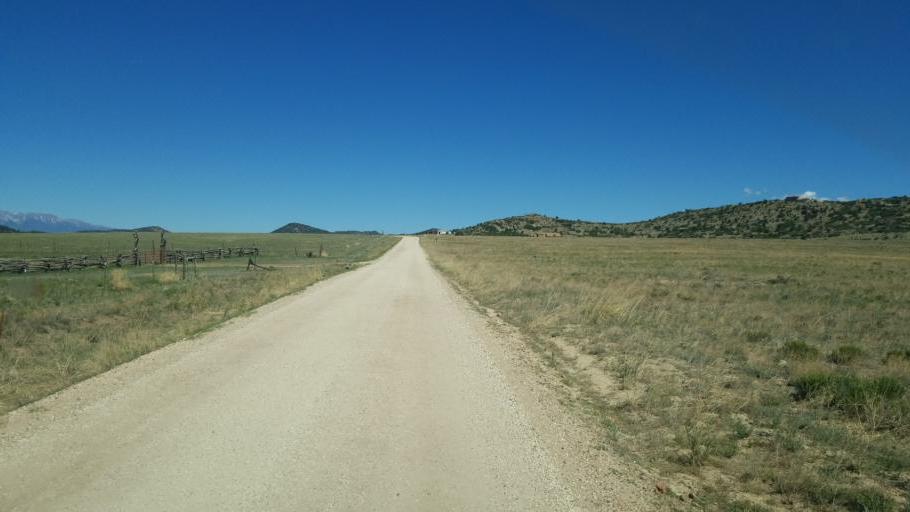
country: US
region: Colorado
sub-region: Custer County
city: Westcliffe
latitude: 38.2364
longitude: -105.4889
